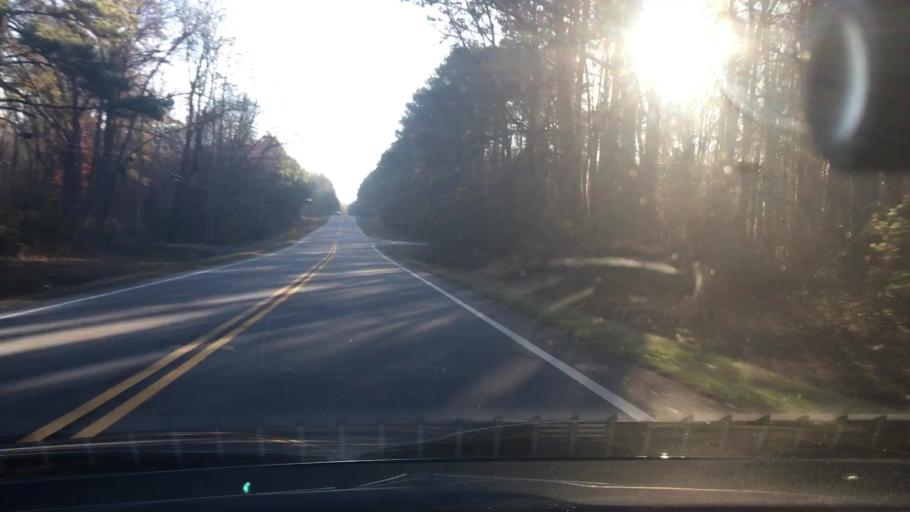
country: US
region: Georgia
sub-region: Coweta County
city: Senoia
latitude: 33.2622
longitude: -84.5161
